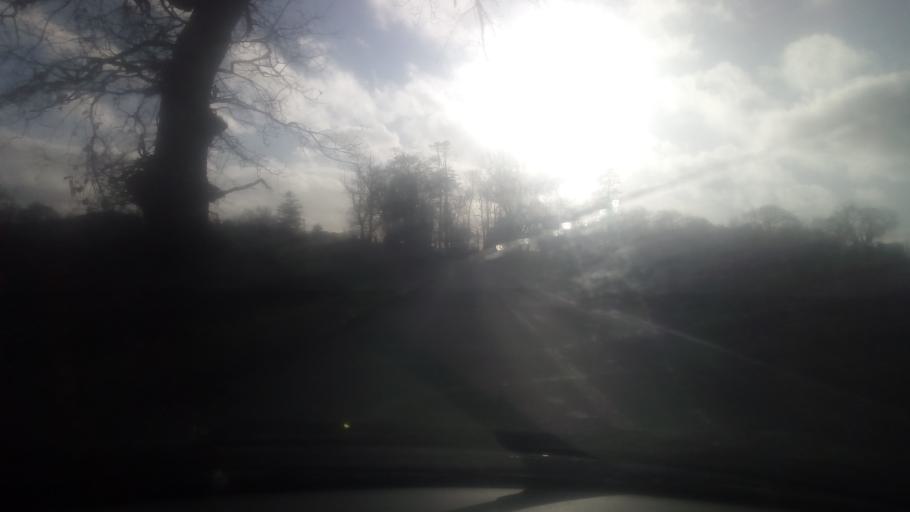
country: GB
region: Scotland
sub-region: The Scottish Borders
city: Duns
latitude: 55.6877
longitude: -2.3430
